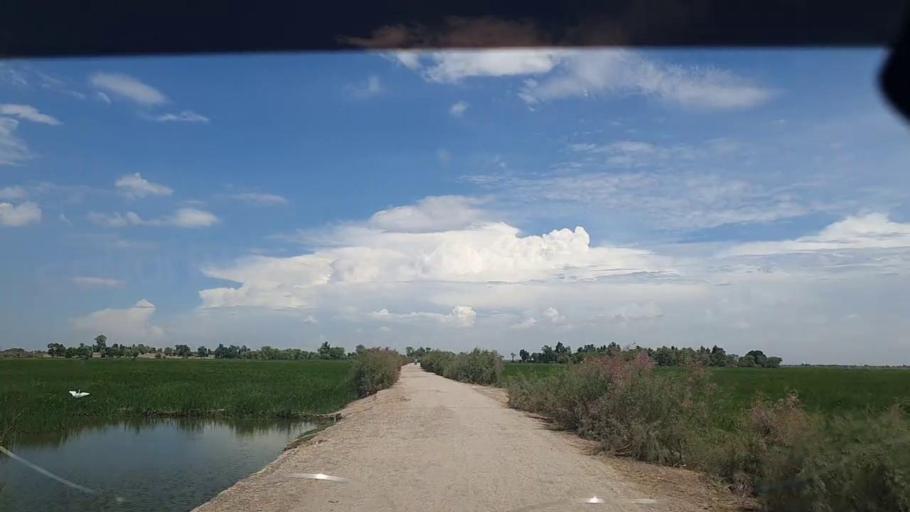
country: PK
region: Sindh
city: Ghauspur
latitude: 28.1488
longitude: 68.9887
